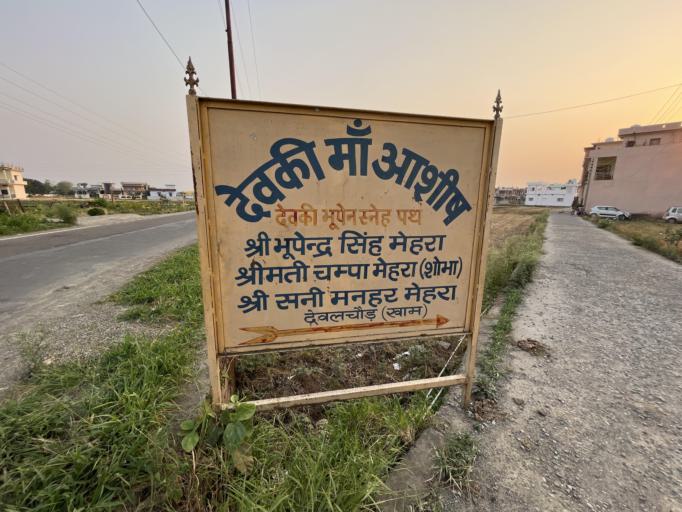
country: IN
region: Uttarakhand
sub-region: Naini Tal
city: Haldwani
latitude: 29.1857
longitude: 79.4938
